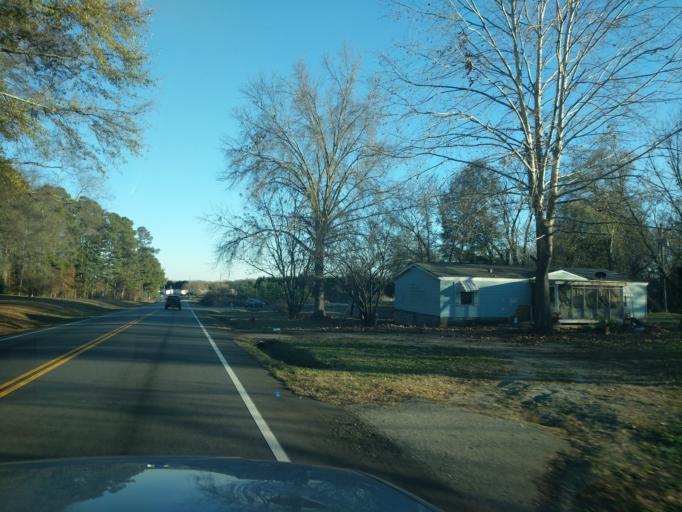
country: US
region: South Carolina
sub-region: Oconee County
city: Seneca
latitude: 34.5954
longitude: -82.9743
